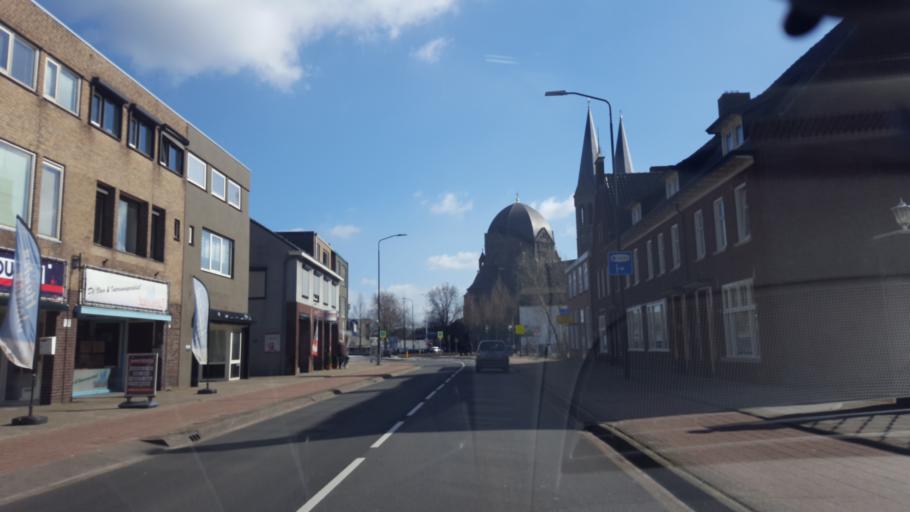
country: NL
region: North Brabant
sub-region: Gemeente Geldrop-Mierlo
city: Geldrop
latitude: 51.4230
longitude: 5.5551
